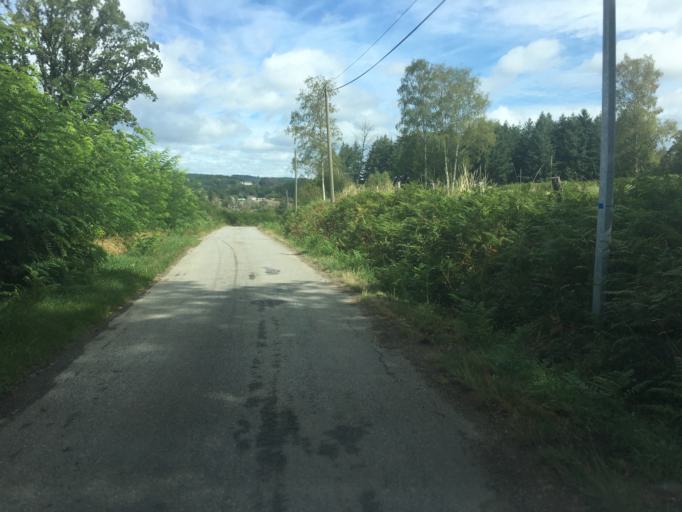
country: FR
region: Auvergne
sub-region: Departement du Cantal
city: Champagnac
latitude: 45.4183
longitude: 2.4064
